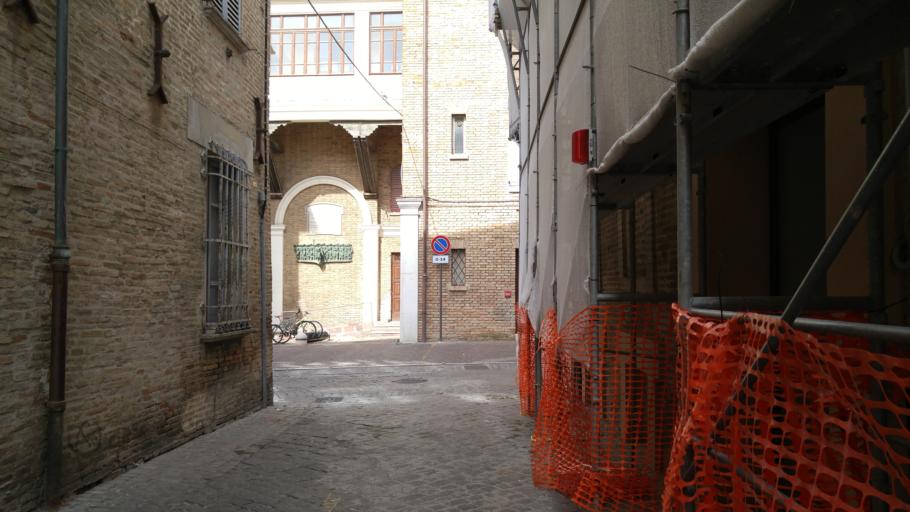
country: IT
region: The Marches
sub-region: Provincia di Ancona
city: Senigallia
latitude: 43.7147
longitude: 13.2176
